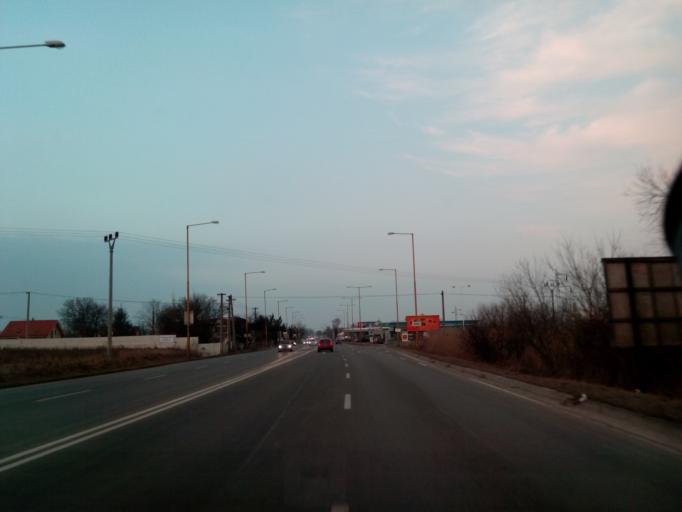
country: SK
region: Kosicky
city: Kosice
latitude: 48.6674
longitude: 21.2719
